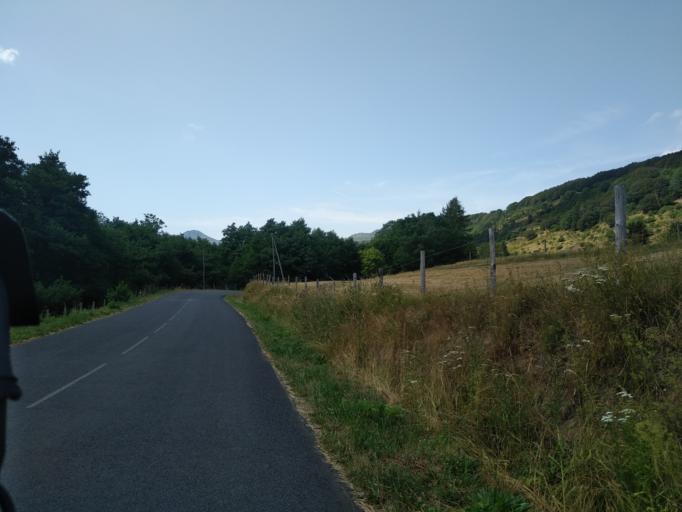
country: FR
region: Auvergne
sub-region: Departement du Cantal
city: Riom-es-Montagnes
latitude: 45.1662
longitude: 2.7109
